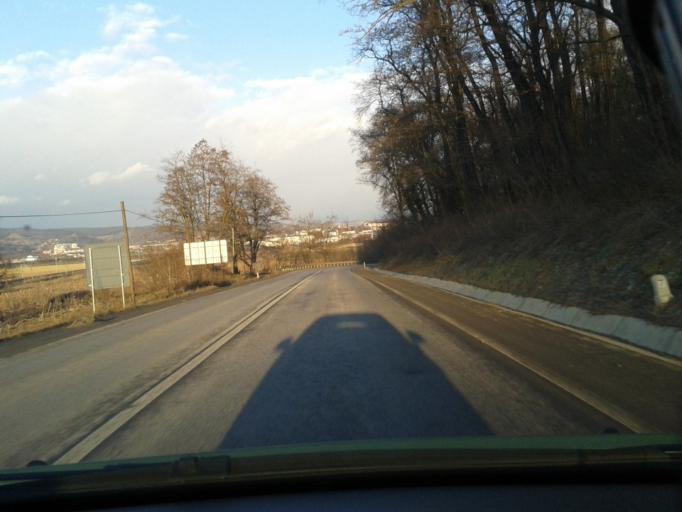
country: RO
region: Sibiu
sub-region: Comuna Tarnava
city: Tarnava
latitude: 46.1404
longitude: 24.3140
